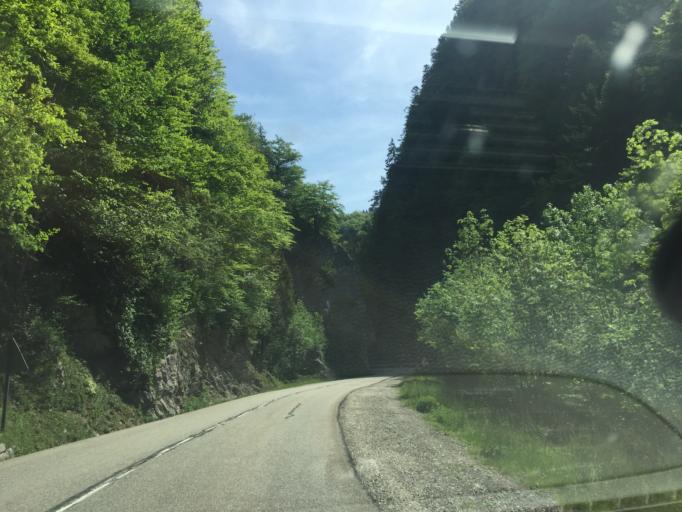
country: FR
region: Rhone-Alpes
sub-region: Departement de l'Isere
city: Saint-Vincent-de-Mercuze
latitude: 45.4336
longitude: 5.8725
